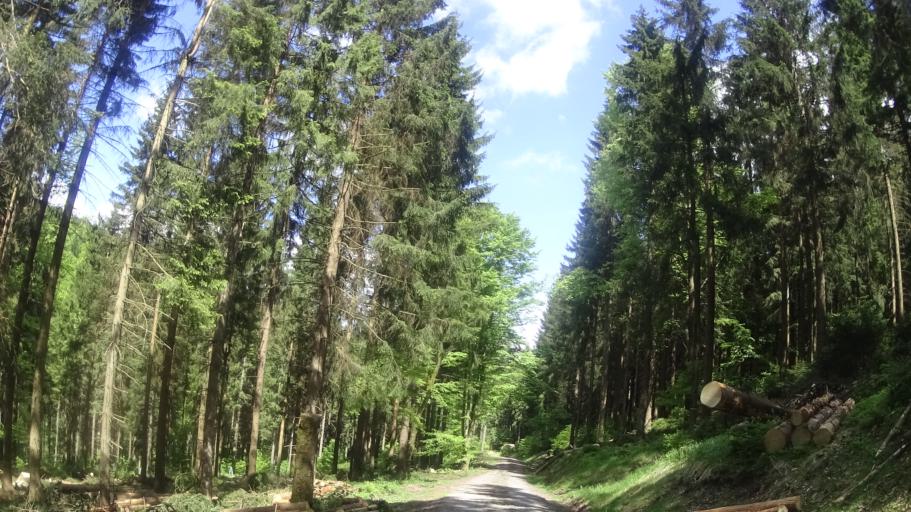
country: DE
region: Thuringia
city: Altenfeld
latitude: 50.5830
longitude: 10.9552
